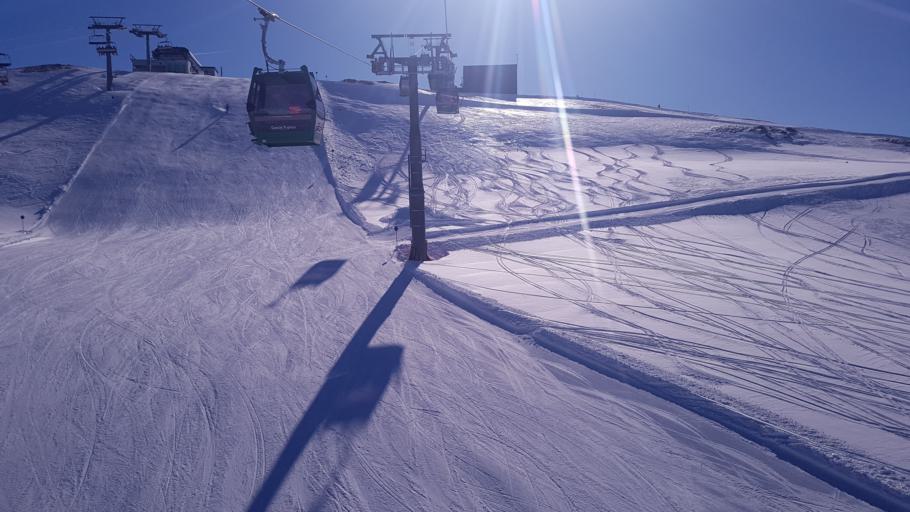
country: AT
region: Salzburg
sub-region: Politischer Bezirk Zell am See
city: Neukirchen am Grossvenediger
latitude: 47.2838
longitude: 12.2867
